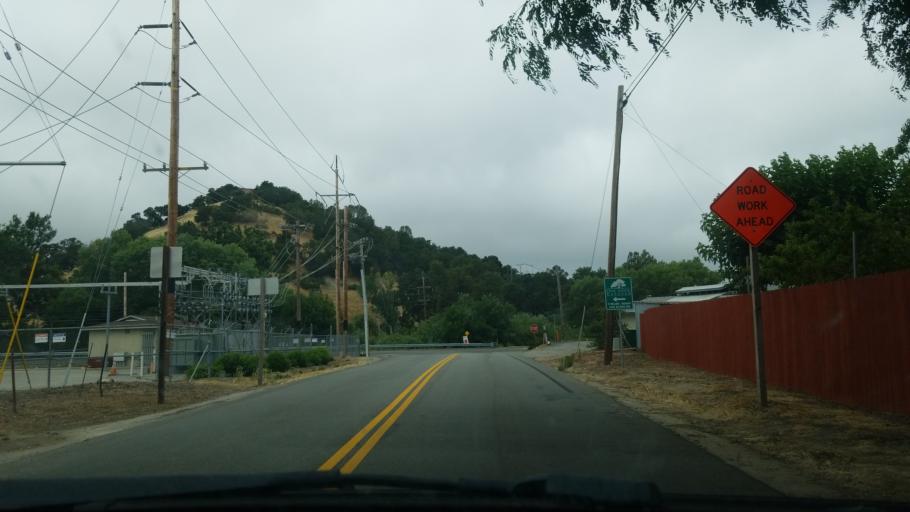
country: US
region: California
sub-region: San Luis Obispo County
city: Atascadero
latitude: 35.4655
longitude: -120.6710
